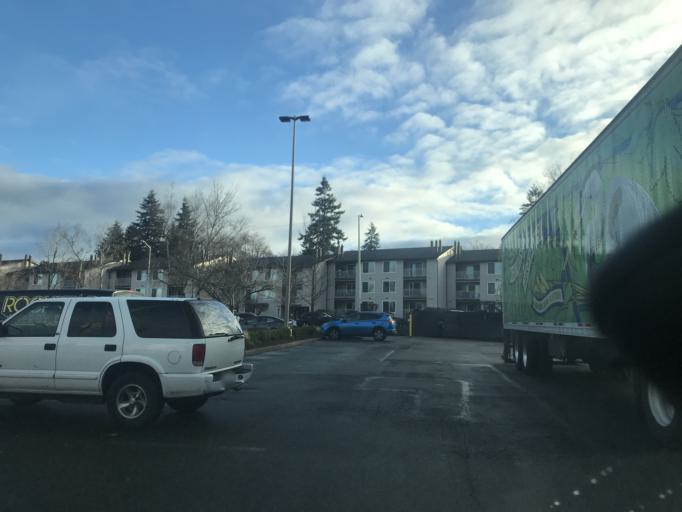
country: US
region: Washington
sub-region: King County
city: White Center
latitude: 47.5217
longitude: -122.3654
